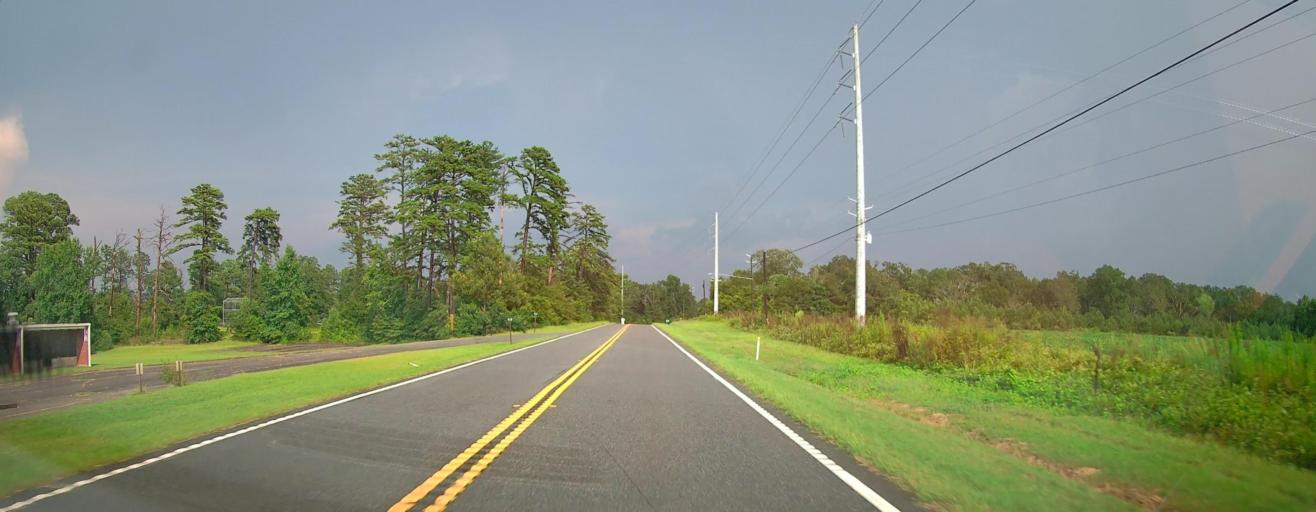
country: US
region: Georgia
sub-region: Twiggs County
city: Jeffersonville
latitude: 32.6013
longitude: -83.2419
